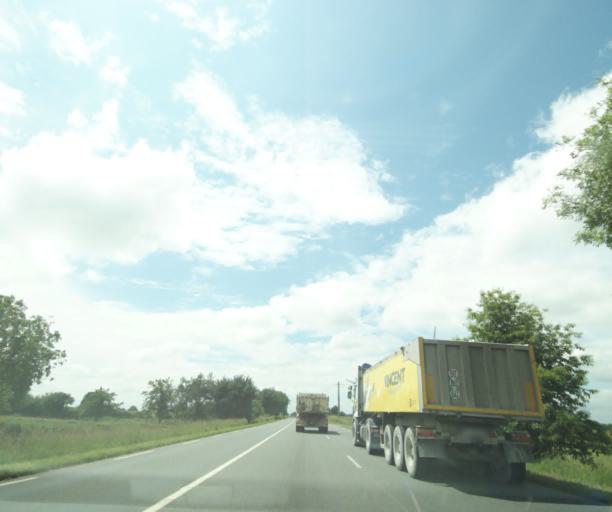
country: FR
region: Poitou-Charentes
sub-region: Departement des Deux-Sevres
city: Champdeniers-Saint-Denis
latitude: 46.4633
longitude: -0.3734
